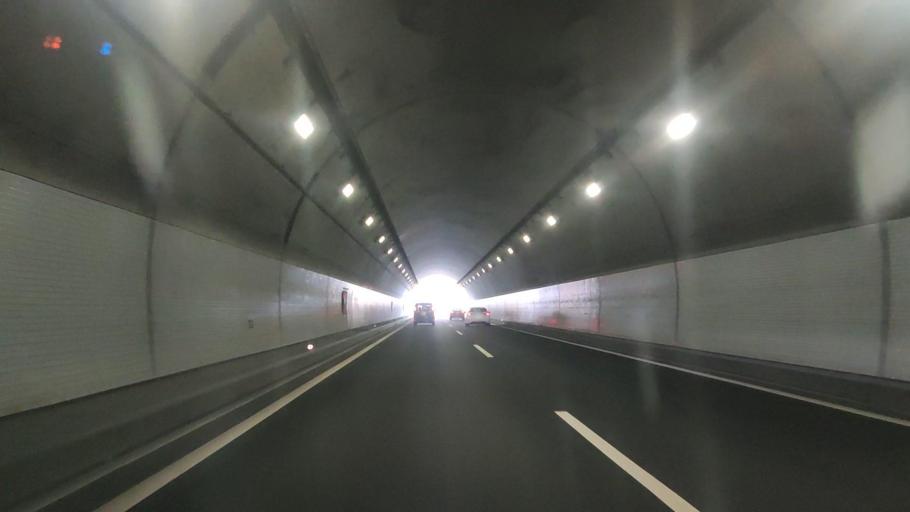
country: JP
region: Fukuoka
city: Kanda
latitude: 33.8118
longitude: 130.9096
